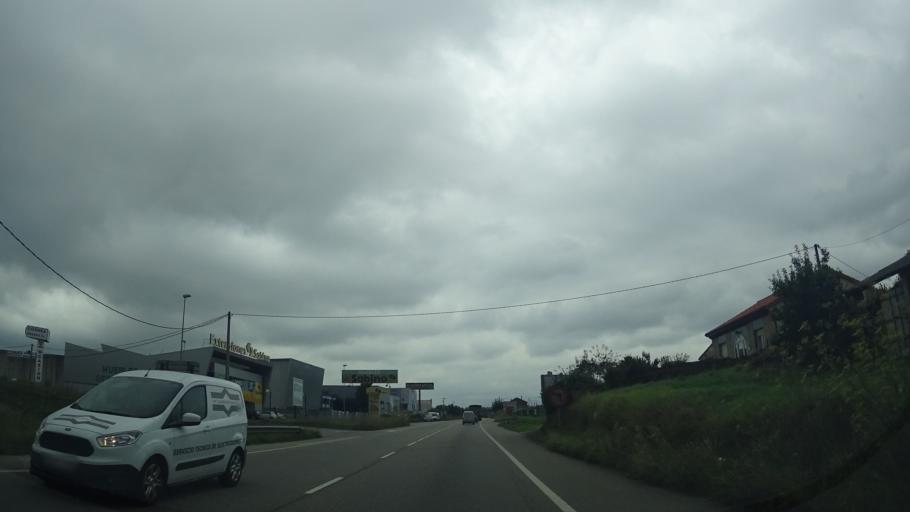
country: ES
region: Asturias
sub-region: Province of Asturias
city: Norena
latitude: 43.3832
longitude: -5.7520
